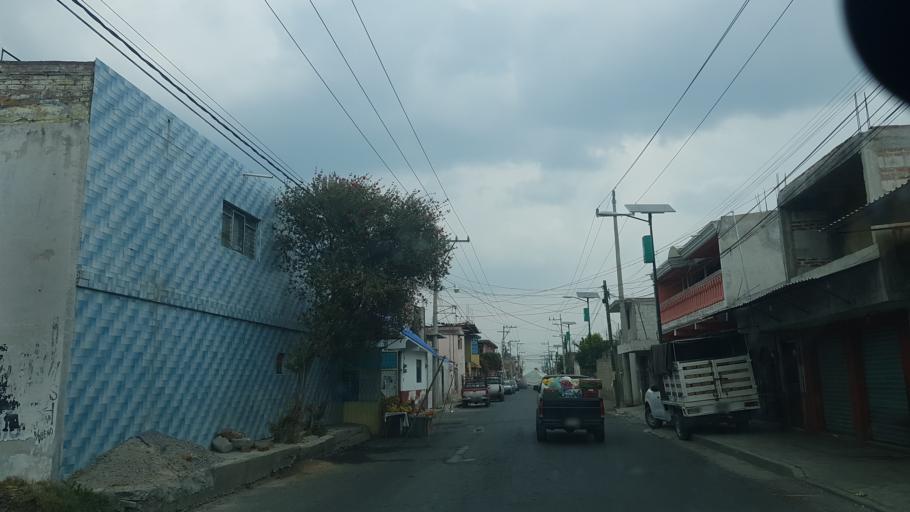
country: MX
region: Puebla
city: Huejotzingo
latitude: 19.1636
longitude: -98.4118
